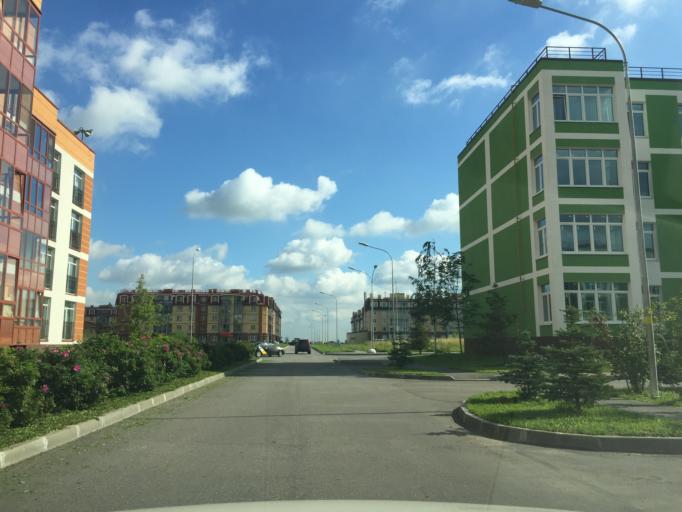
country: RU
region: St.-Petersburg
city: Aleksandrovskaya
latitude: 59.7540
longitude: 30.3683
